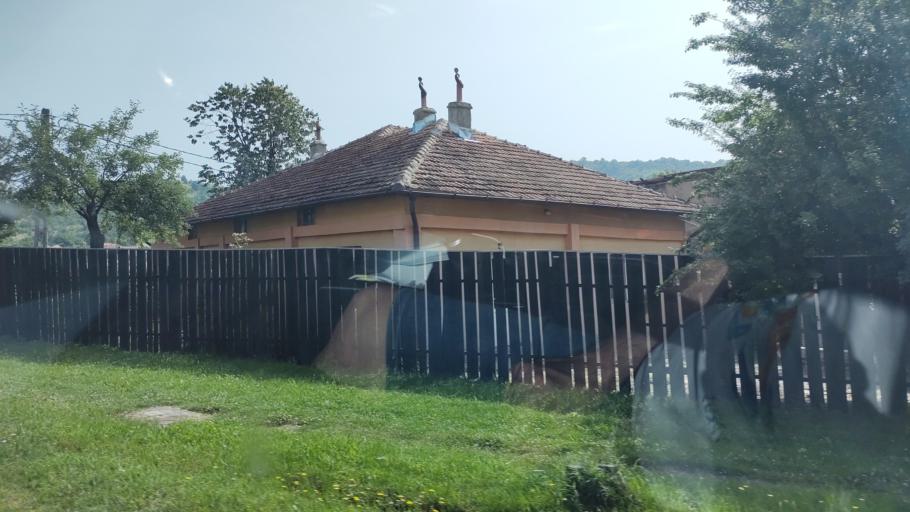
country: RO
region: Mehedinti
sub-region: Comuna Eselnita
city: Eselnita
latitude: 44.7017
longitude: 22.3617
